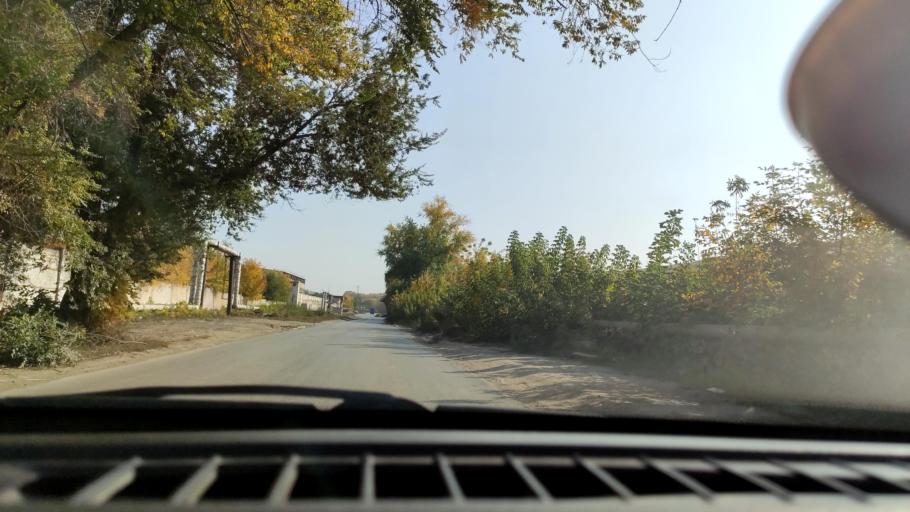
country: RU
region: Samara
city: Samara
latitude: 53.1947
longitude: 50.2613
